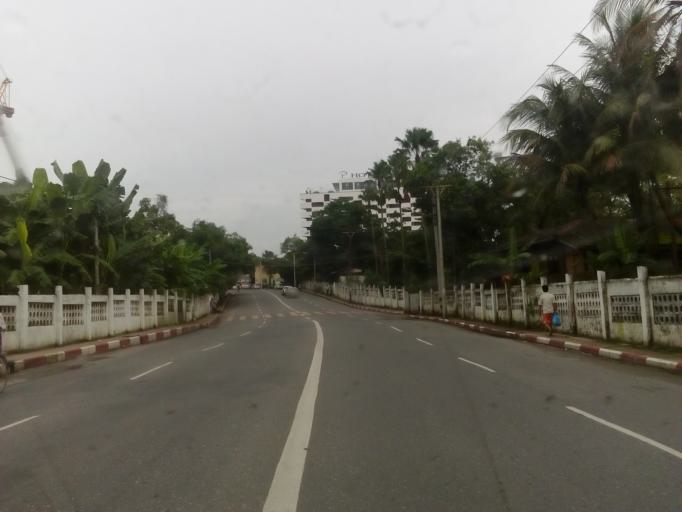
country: MM
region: Yangon
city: Yangon
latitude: 16.8505
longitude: 96.1536
